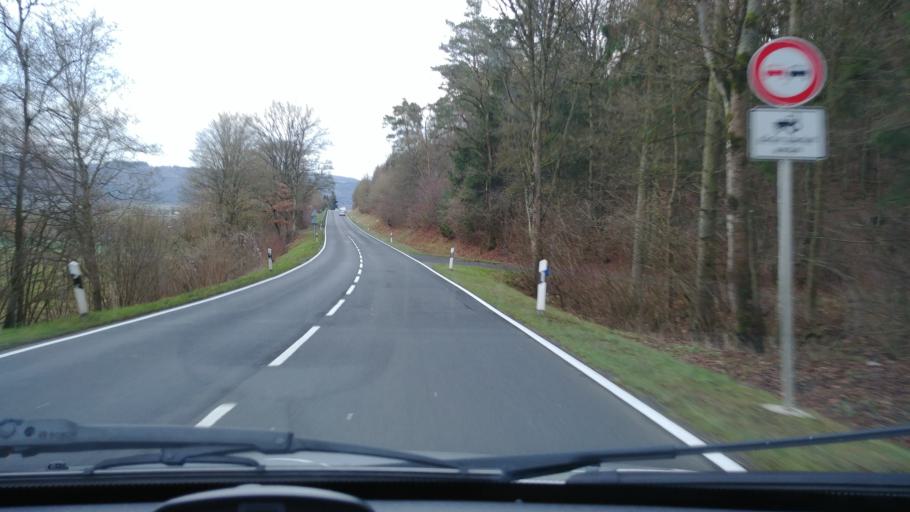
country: DE
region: Bavaria
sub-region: Regierungsbezirk Unterfranken
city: Steinfeld
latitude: 49.9813
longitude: 9.7182
